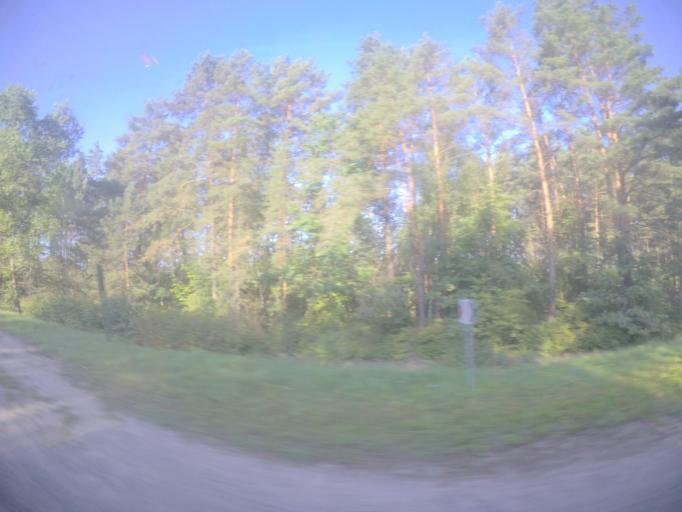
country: BY
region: Grodnenskaya
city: Hrodna
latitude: 53.8479
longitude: 23.8903
